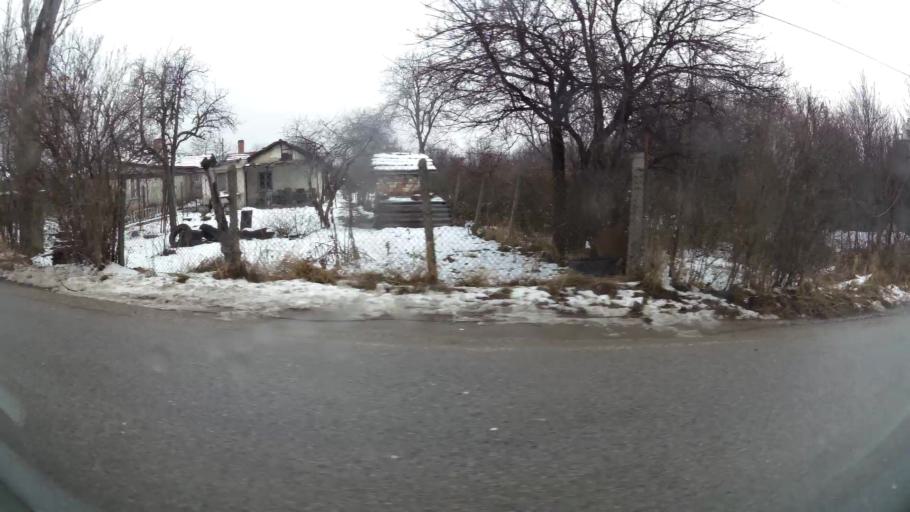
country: BG
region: Sofia-Capital
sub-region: Stolichna Obshtina
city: Sofia
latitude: 42.6555
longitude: 23.2974
